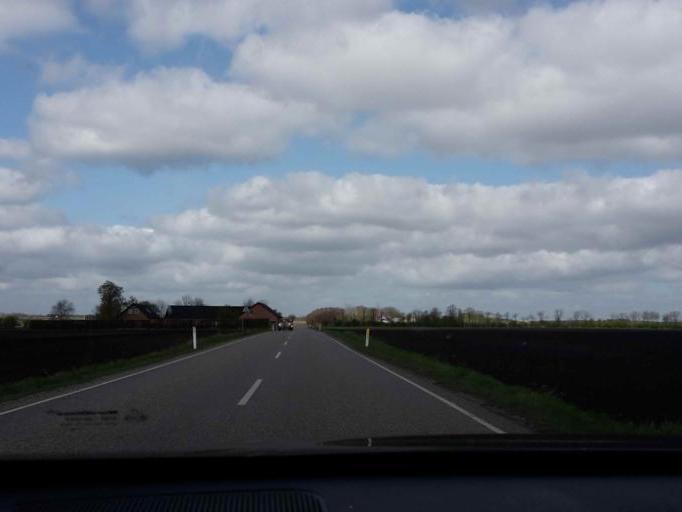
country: DK
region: South Denmark
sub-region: Varde Kommune
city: Olgod
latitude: 55.7886
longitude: 8.6938
